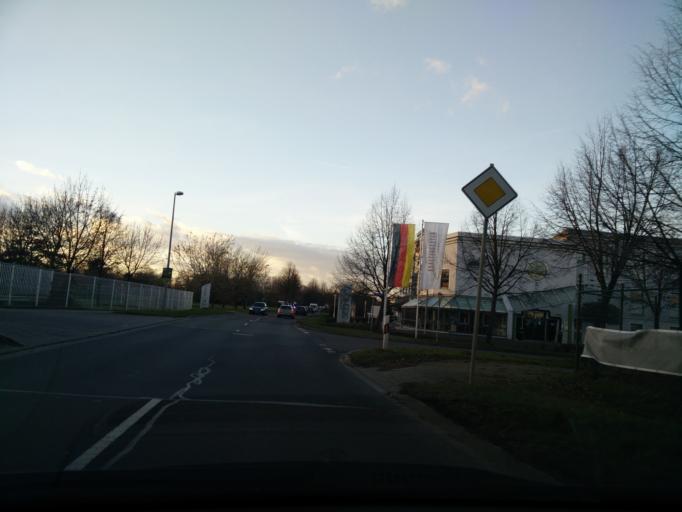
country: DE
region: Saxony
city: Zwenkau
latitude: 51.2157
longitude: 12.3419
